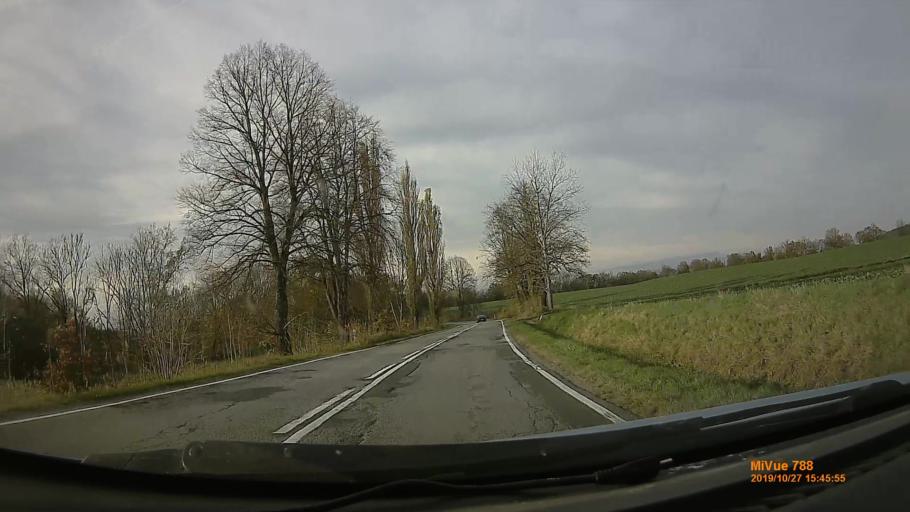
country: PL
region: Lower Silesian Voivodeship
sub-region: Powiat klodzki
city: Bozkow
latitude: 50.4778
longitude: 16.5906
